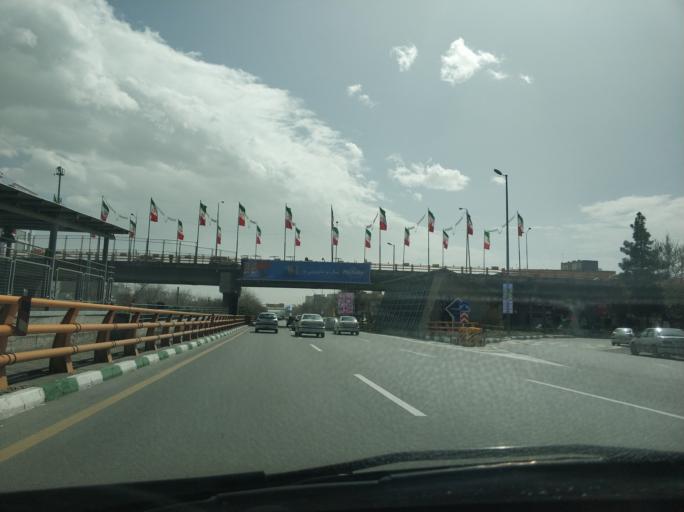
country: IR
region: Razavi Khorasan
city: Mashhad
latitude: 36.3275
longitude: 59.5005
